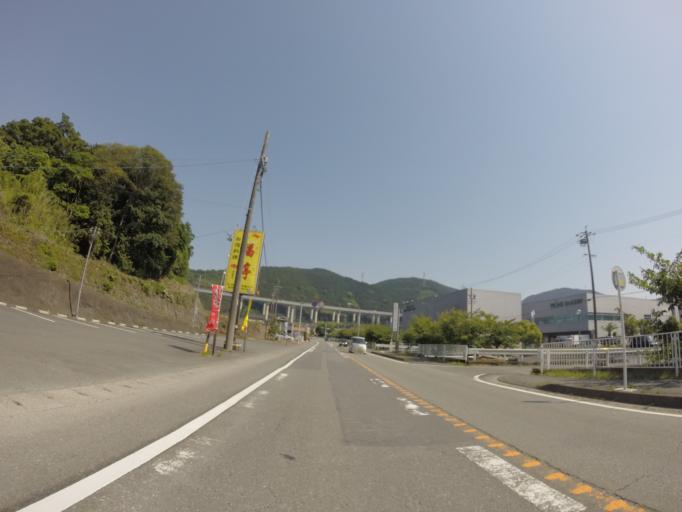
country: JP
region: Shizuoka
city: Fujinomiya
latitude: 35.1831
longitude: 138.6031
